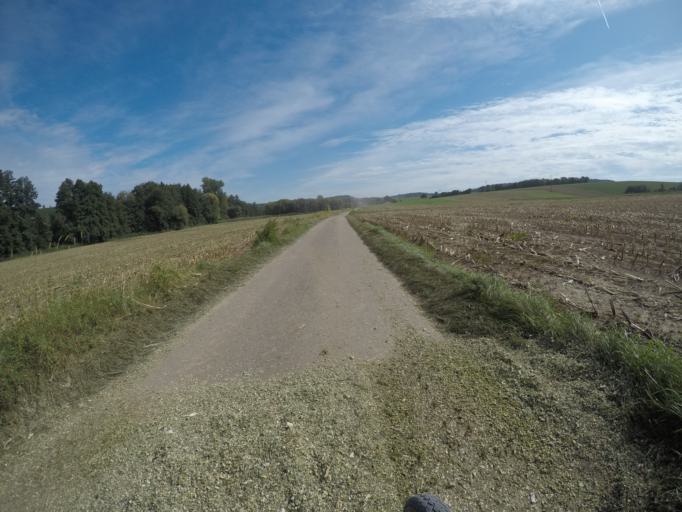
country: DE
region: Baden-Wuerttemberg
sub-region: Karlsruhe Region
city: Oberderdingen
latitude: 49.0777
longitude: 8.8161
